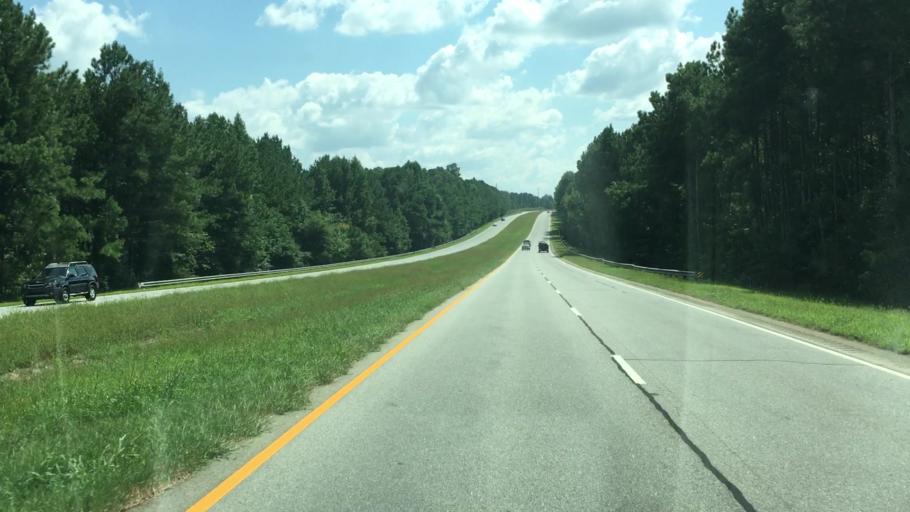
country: US
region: Georgia
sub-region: Morgan County
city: Madison
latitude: 33.5879
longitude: -83.4465
